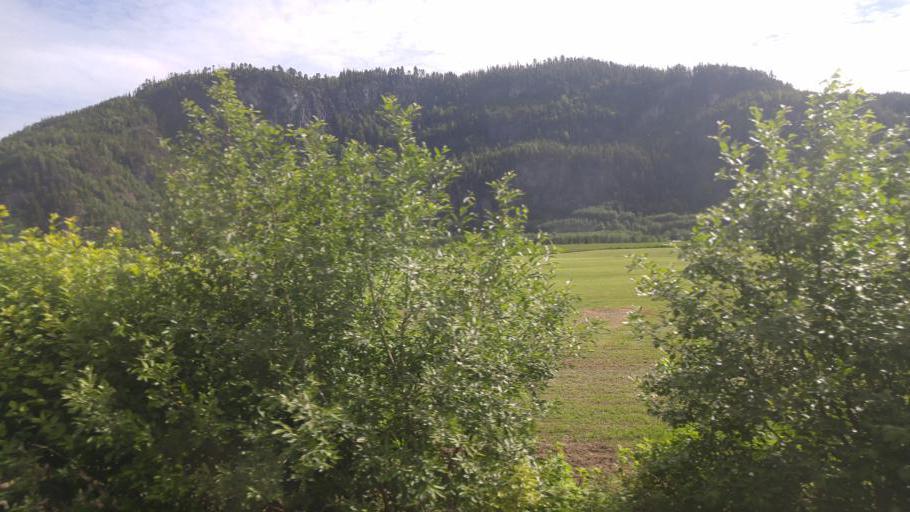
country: NO
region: Sor-Trondelag
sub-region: Midtre Gauldal
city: Storen
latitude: 63.0474
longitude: 10.2862
